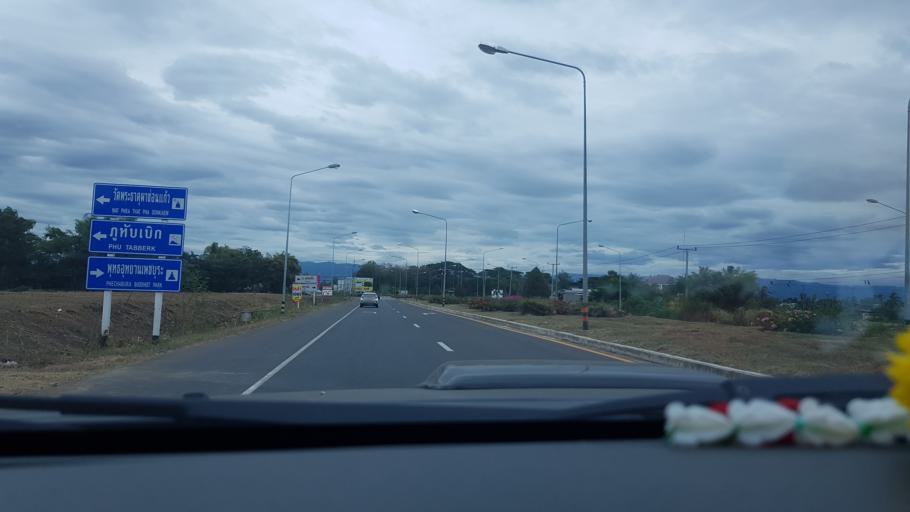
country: TH
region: Phetchabun
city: Phetchabun
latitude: 16.4973
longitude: 101.1552
